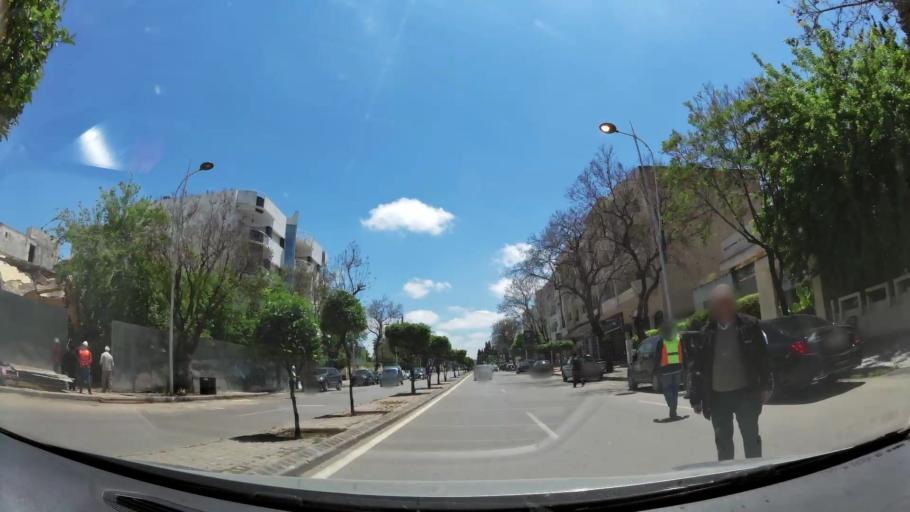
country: MA
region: Fes-Boulemane
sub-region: Fes
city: Fes
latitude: 34.0254
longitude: -4.9978
